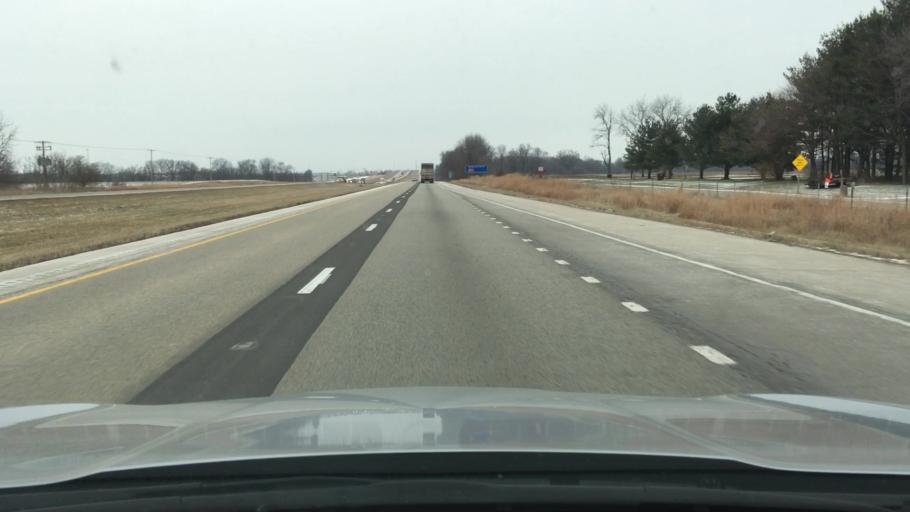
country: US
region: Illinois
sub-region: Sangamon County
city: Divernon
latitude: 39.5736
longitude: -89.6461
